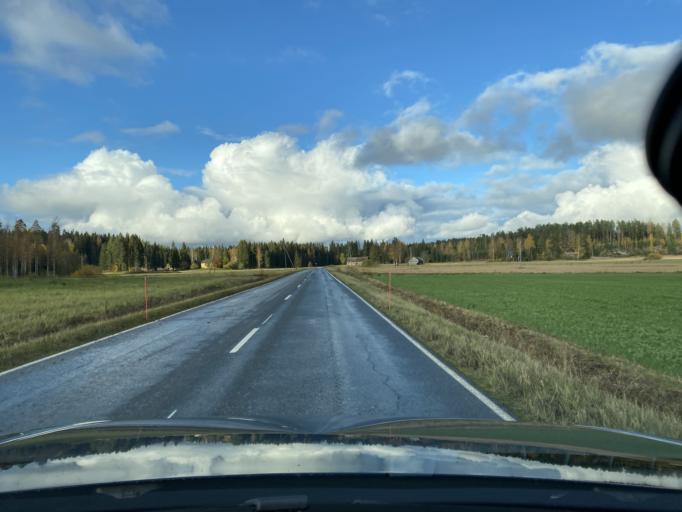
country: FI
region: Haeme
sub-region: Forssa
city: Humppila
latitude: 60.9849
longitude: 23.2536
